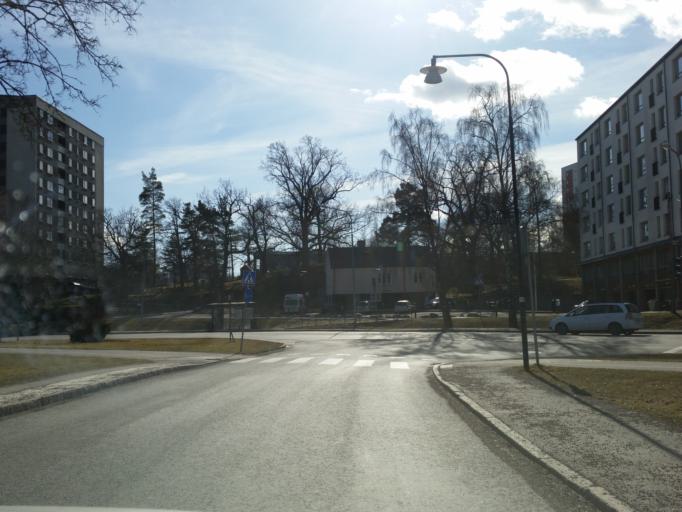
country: SE
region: Stockholm
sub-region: Sundbybergs Kommun
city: Sundbyberg
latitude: 59.3683
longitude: 17.9495
